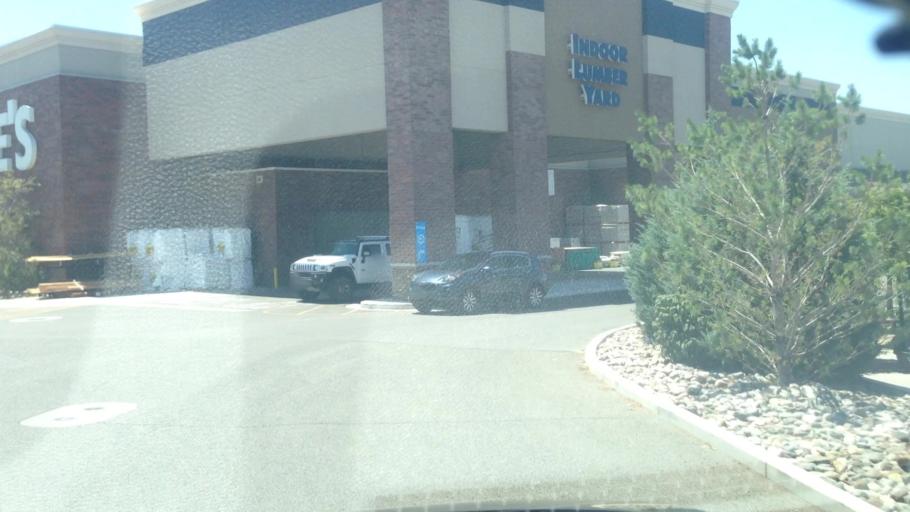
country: US
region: Nevada
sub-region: Washoe County
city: Sparks
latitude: 39.5311
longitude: -119.7172
